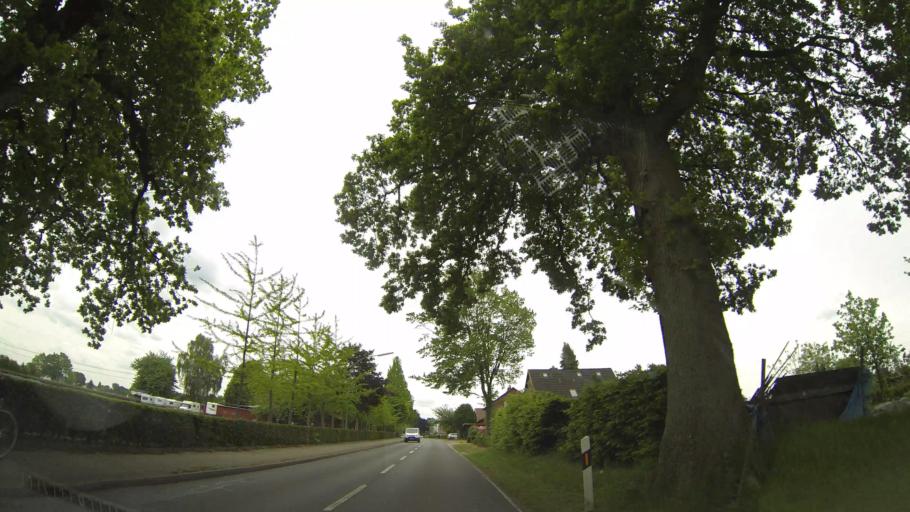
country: DE
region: Schleswig-Holstein
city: Ellerbek
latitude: 53.6360
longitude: 9.8716
